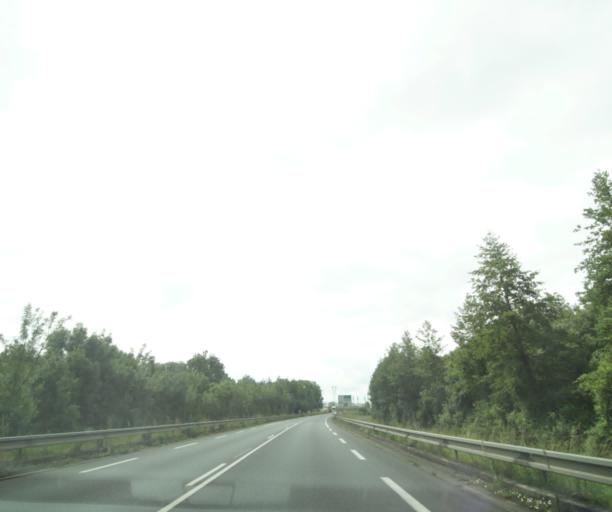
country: FR
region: Pays de la Loire
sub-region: Departement de Maine-et-Loire
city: Distre
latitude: 47.2171
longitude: -0.1163
